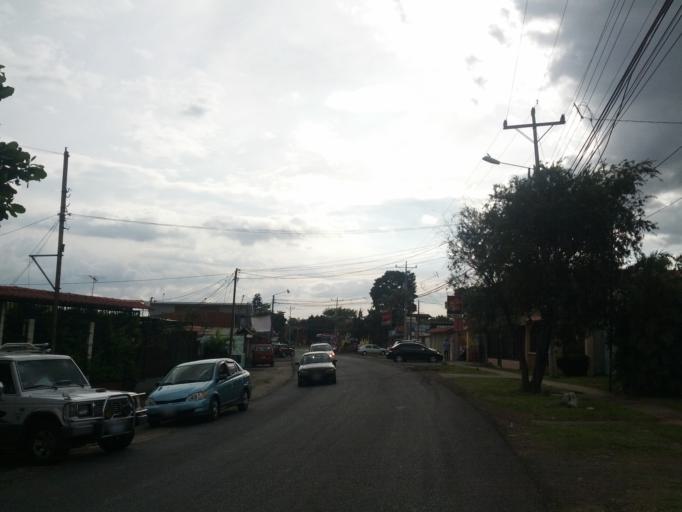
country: CR
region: Alajuela
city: Alajuela
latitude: 10.0272
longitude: -84.1834
